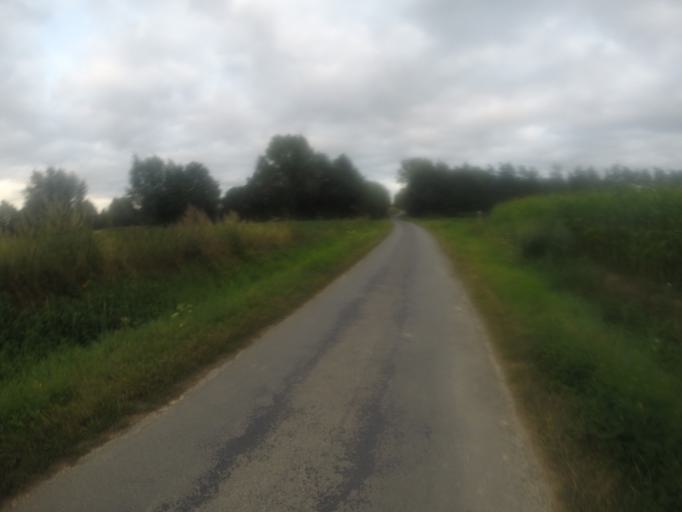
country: BE
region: Flanders
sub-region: Provincie West-Vlaanderen
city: Poperinge
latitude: 50.8455
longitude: 2.7065
